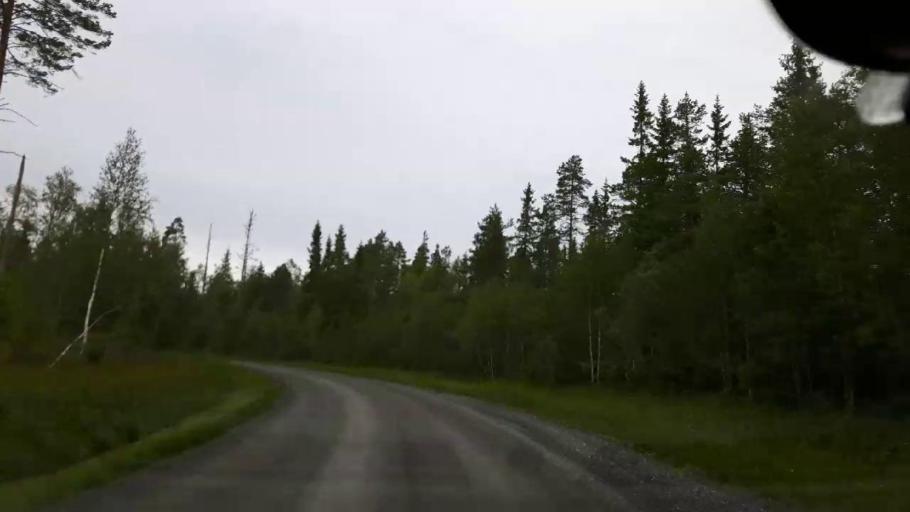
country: SE
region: Jaemtland
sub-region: Krokoms Kommun
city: Krokom
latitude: 63.2889
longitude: 14.3825
